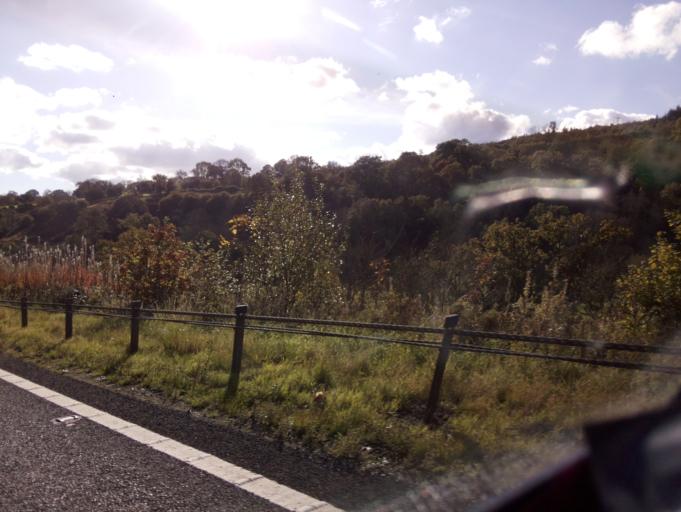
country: GB
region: Wales
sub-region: Merthyr Tydfil County Borough
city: Merthyr Tydfil
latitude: 51.7720
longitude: -3.4177
